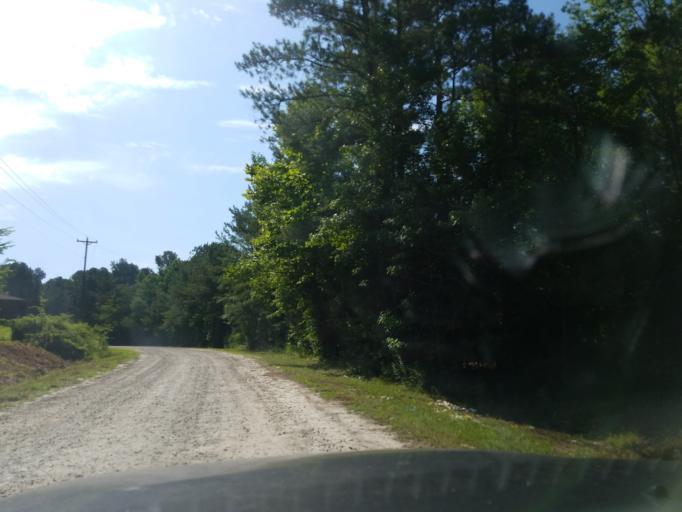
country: US
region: North Carolina
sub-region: Vance County
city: Henderson
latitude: 36.3403
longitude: -78.4185
